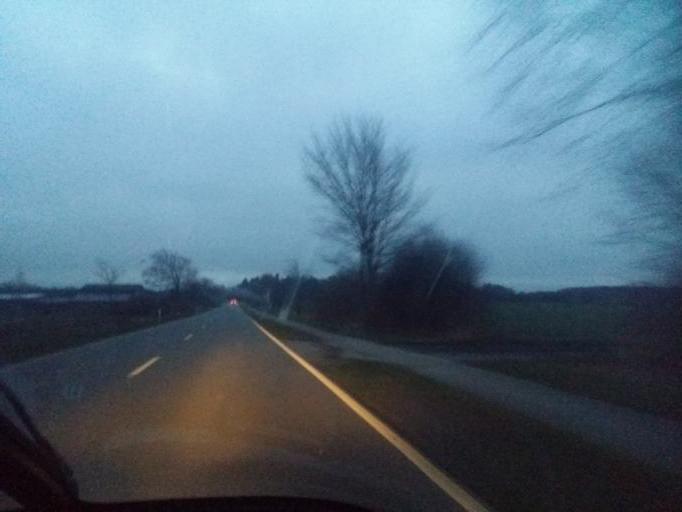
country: DE
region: Schleswig-Holstein
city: Poschendorf
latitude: 54.0299
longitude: 9.4773
